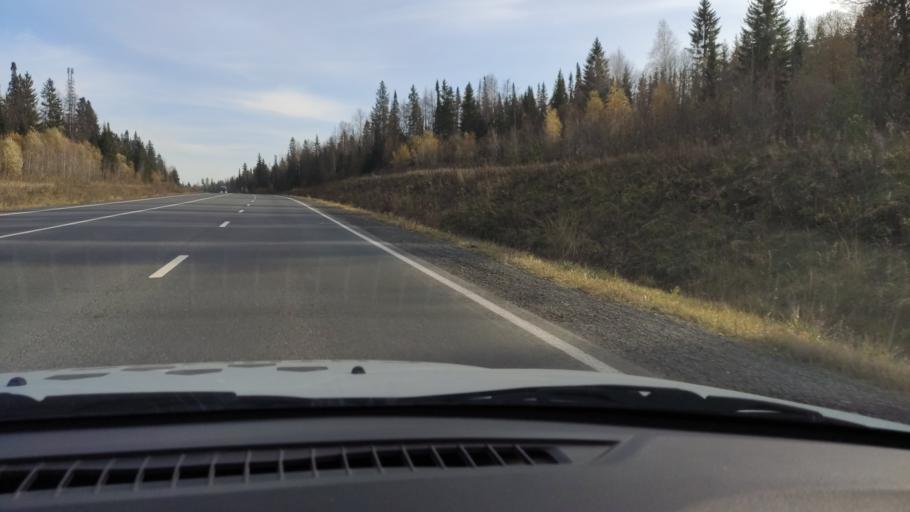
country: RU
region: Perm
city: Novyye Lyady
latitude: 58.0328
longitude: 56.4801
